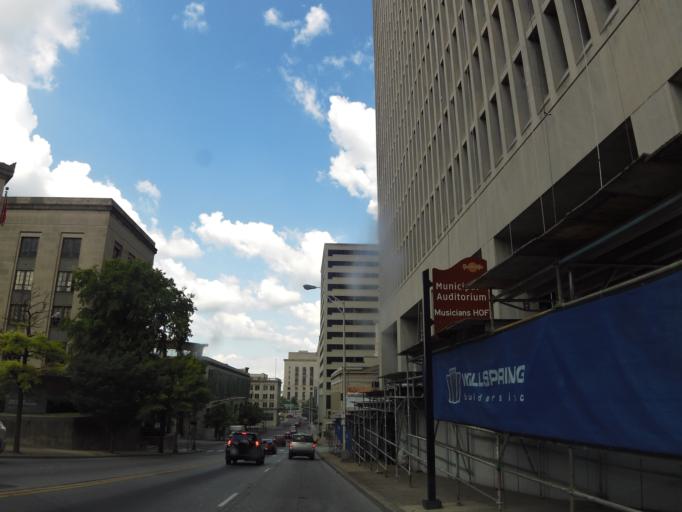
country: US
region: Tennessee
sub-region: Davidson County
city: Nashville
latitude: 36.1655
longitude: -86.7826
